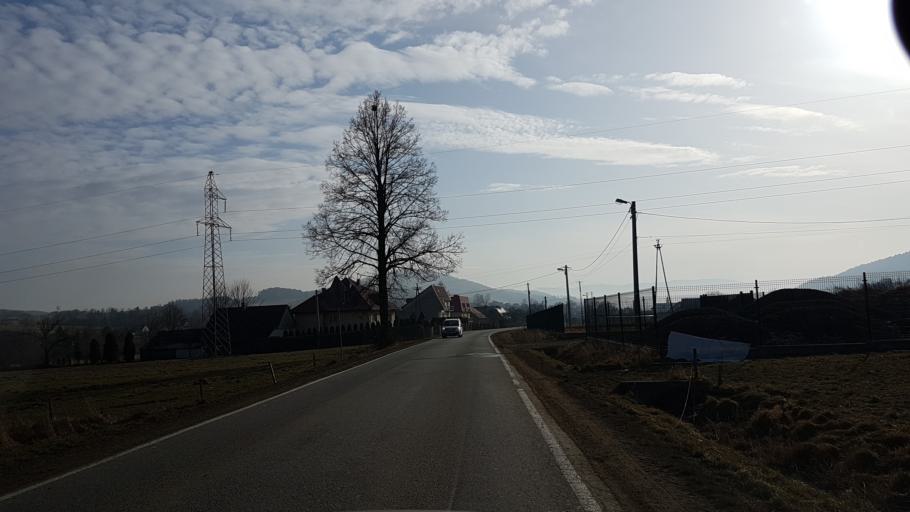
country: PL
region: Lesser Poland Voivodeship
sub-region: Powiat limanowski
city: Lukowica
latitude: 49.6485
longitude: 20.5035
